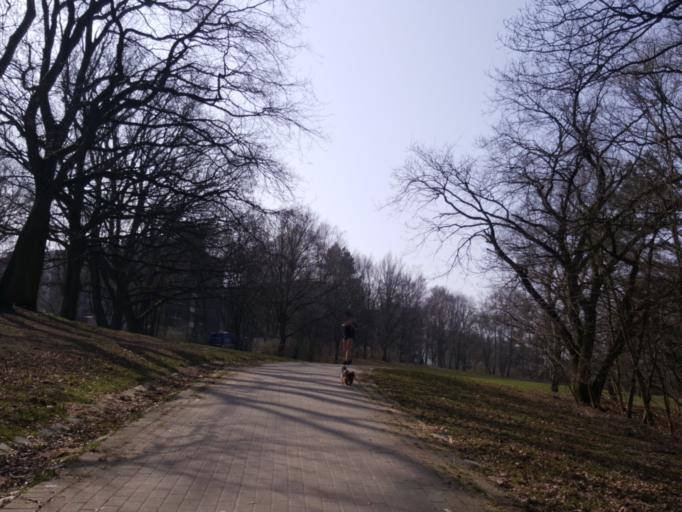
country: DE
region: Schleswig-Holstein
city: Oststeinbek
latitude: 53.5349
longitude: 10.1435
